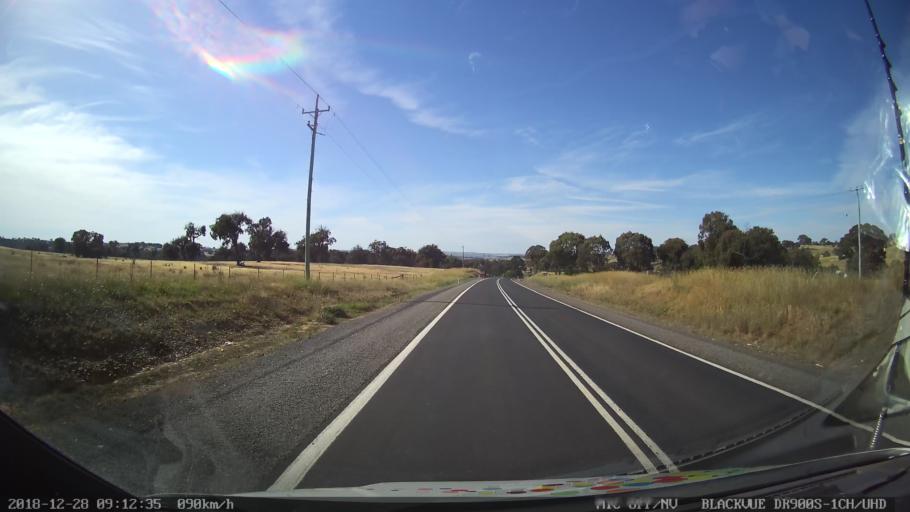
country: AU
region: New South Wales
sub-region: Upper Lachlan Shire
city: Crookwell
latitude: -34.2573
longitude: 149.3424
